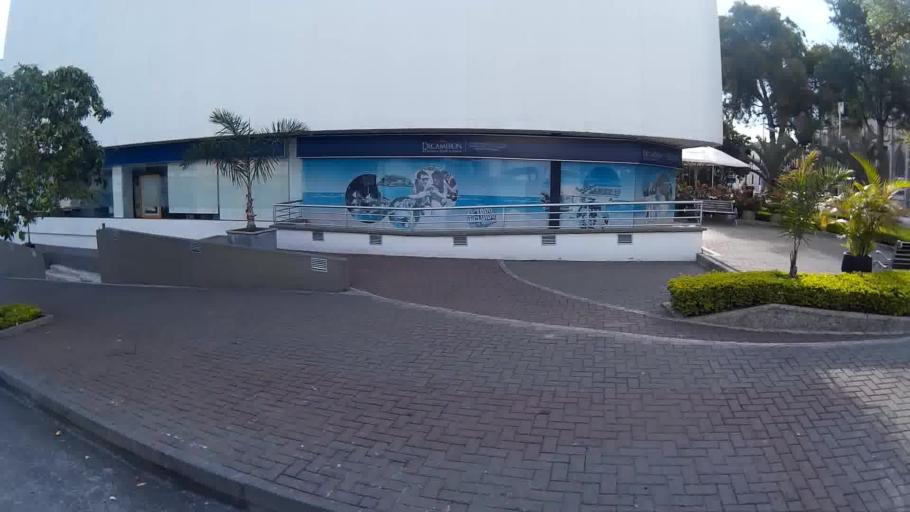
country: CO
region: Risaralda
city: Pereira
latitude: 4.8088
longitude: -75.6912
